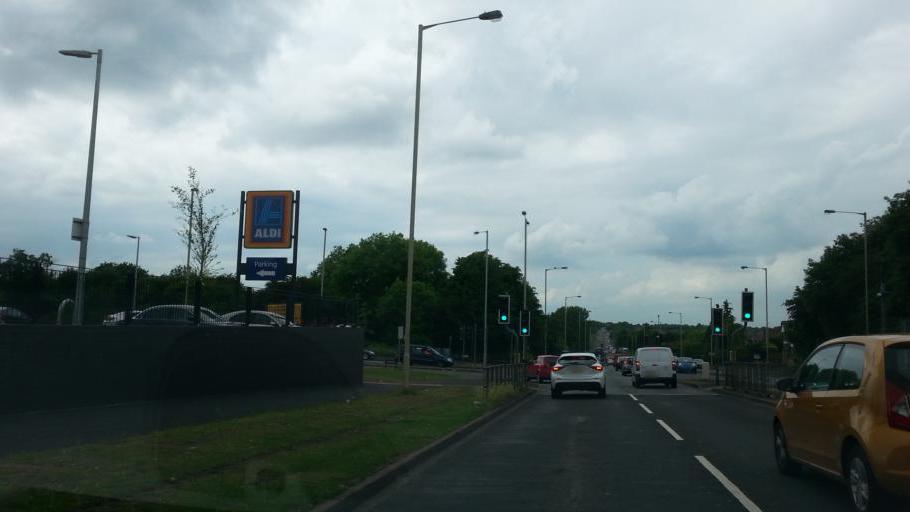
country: GB
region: England
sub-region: Sandwell
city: Tipton
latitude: 52.5272
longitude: -2.0848
